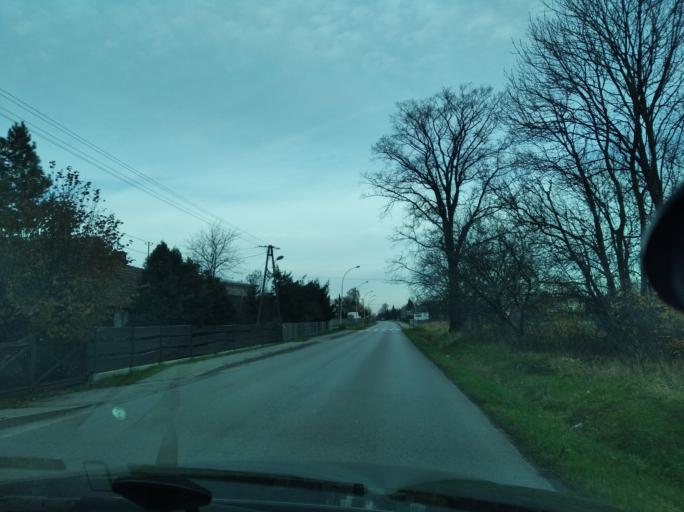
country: PL
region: Subcarpathian Voivodeship
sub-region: Powiat przeworski
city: Przeworsk
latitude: 50.0537
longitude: 22.4734
